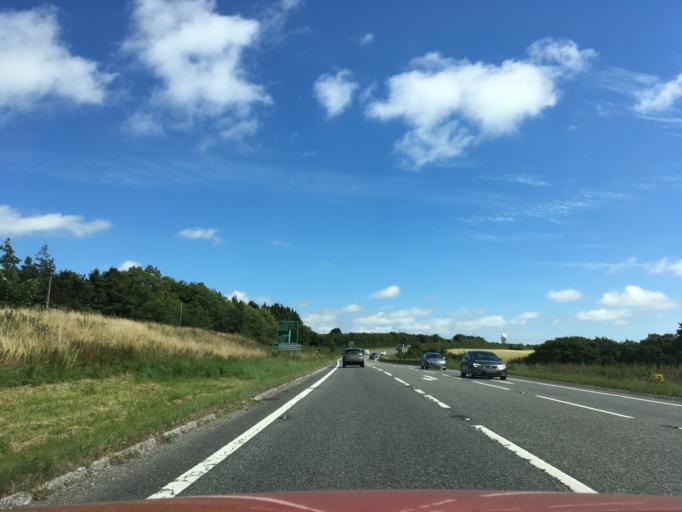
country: GB
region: England
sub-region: Dorset
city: Sherborne
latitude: 50.8251
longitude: -2.5613
